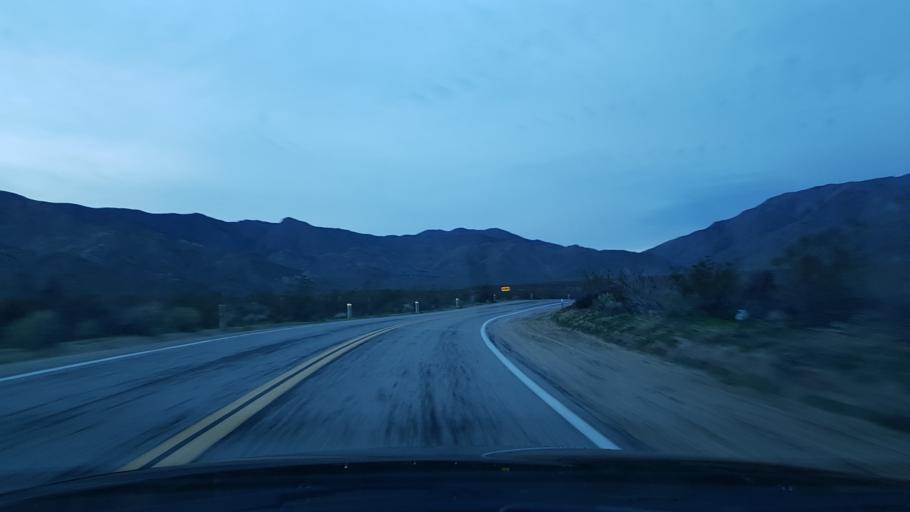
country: US
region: California
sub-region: San Diego County
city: Pine Valley
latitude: 32.9806
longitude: -116.4392
